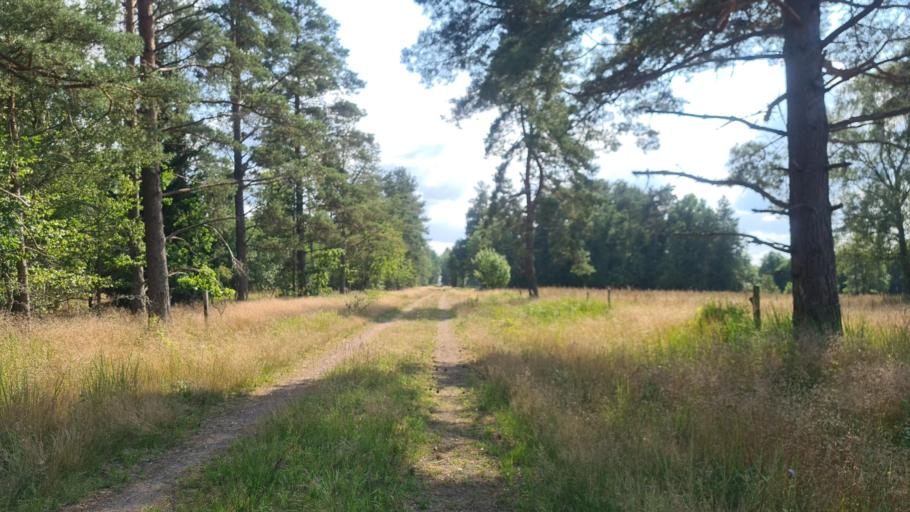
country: SE
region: Kronoberg
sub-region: Ljungby Kommun
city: Ljungby
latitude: 56.7675
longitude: 13.8950
